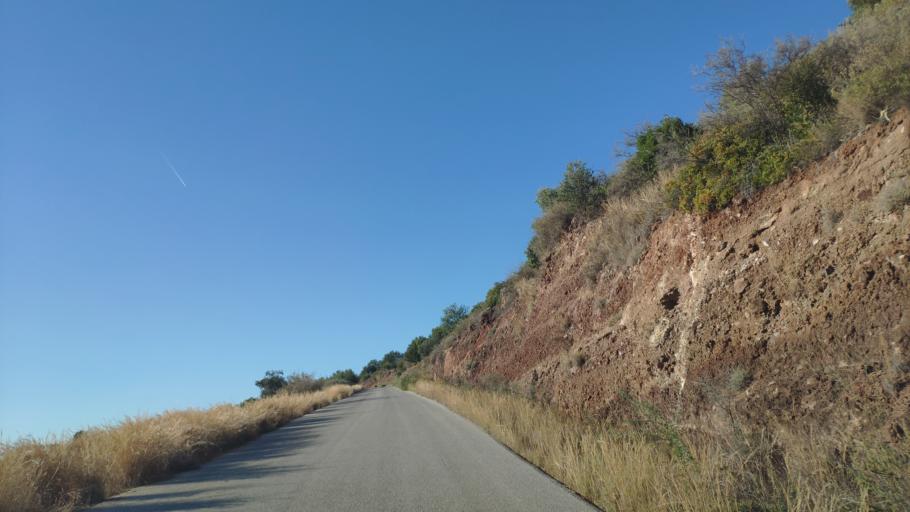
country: GR
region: Attica
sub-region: Nomos Piraios
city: Galatas
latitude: 37.5787
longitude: 23.3545
